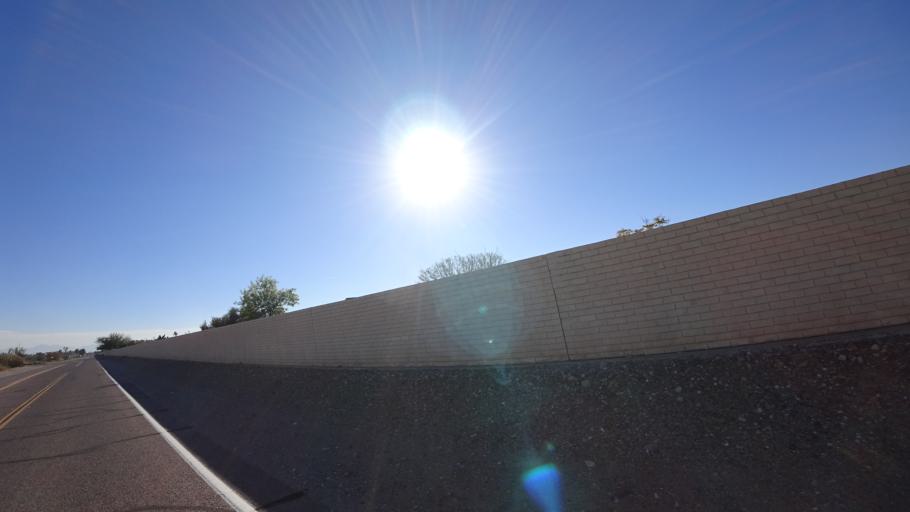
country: US
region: Arizona
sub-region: Maricopa County
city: Surprise
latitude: 33.6475
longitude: -112.3250
